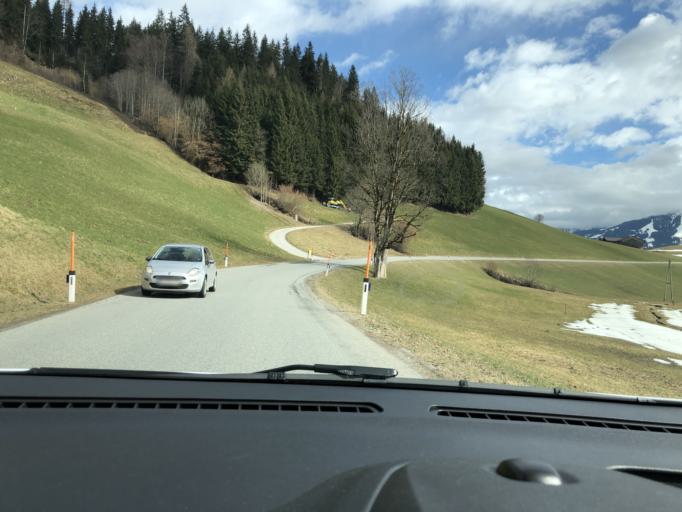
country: AT
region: Tyrol
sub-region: Politischer Bezirk Kitzbuhel
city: Itter
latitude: 47.4494
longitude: 12.1180
